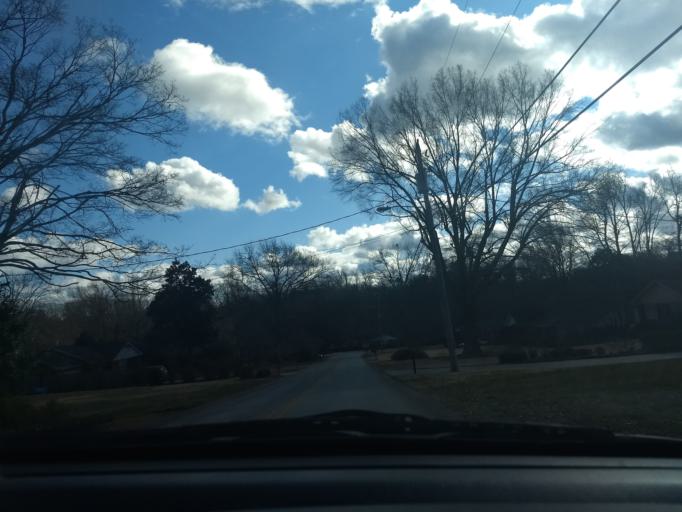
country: US
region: South Carolina
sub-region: Greenville County
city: Wade Hampton
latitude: 34.8770
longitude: -82.3549
